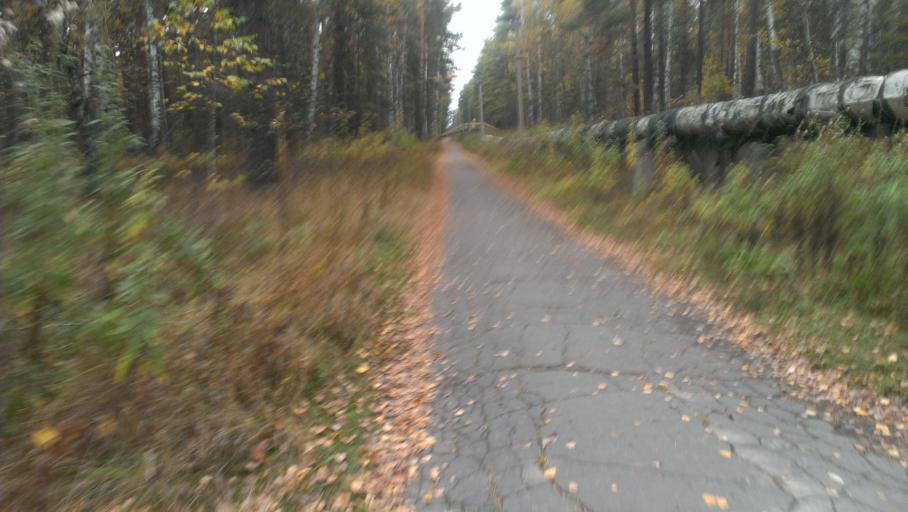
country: RU
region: Altai Krai
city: Yuzhnyy
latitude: 53.2635
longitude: 83.6861
